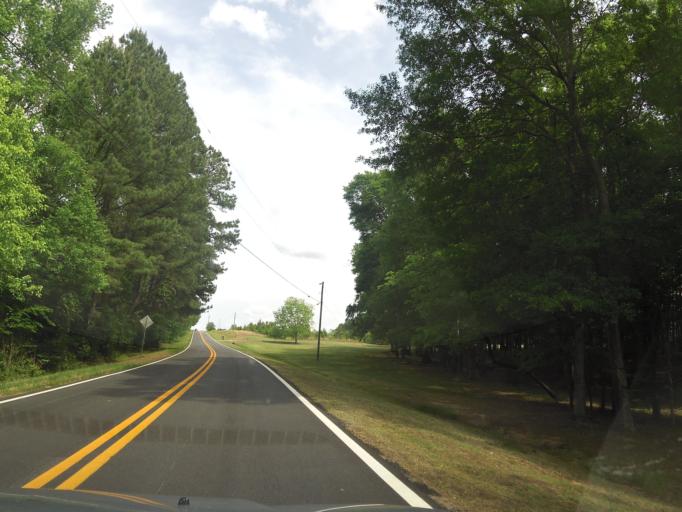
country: US
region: Georgia
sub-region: McDuffie County
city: Thomson
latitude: 33.5305
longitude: -82.4834
